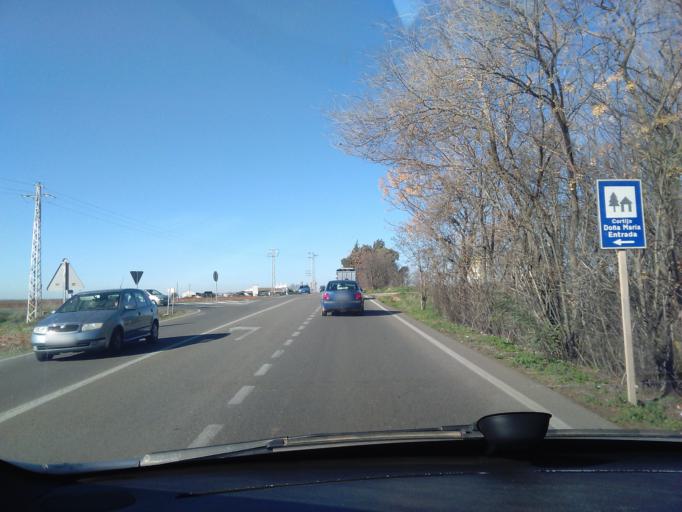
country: ES
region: Andalusia
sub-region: Provincia de Sevilla
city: Sevilla
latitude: 37.4325
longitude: -5.9368
